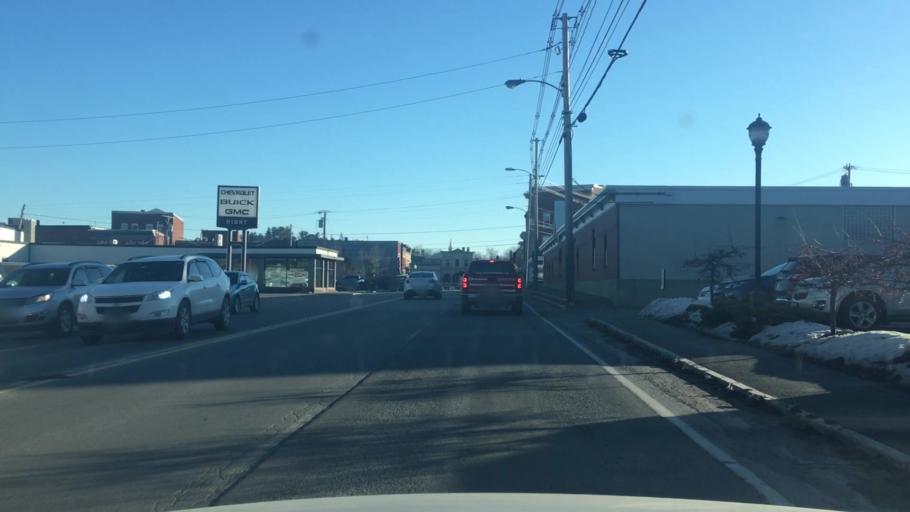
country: US
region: Maine
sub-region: Somerset County
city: Skowhegan
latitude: 44.7668
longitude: -69.7202
